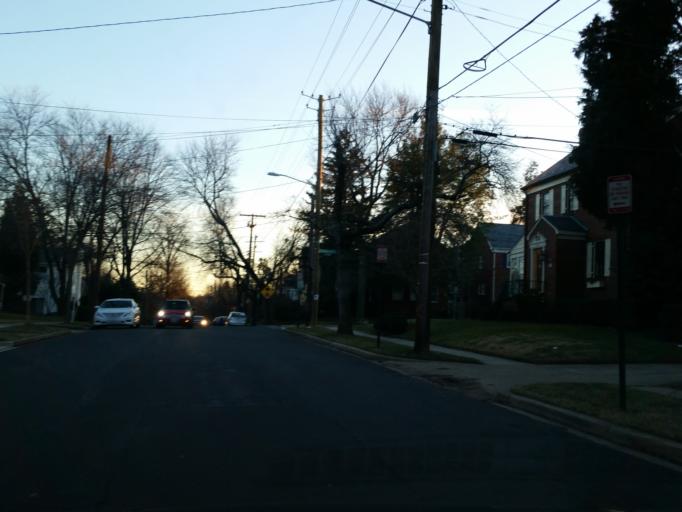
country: US
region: Maryland
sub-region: Montgomery County
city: Friendship Village
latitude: 38.9558
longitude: -77.0862
